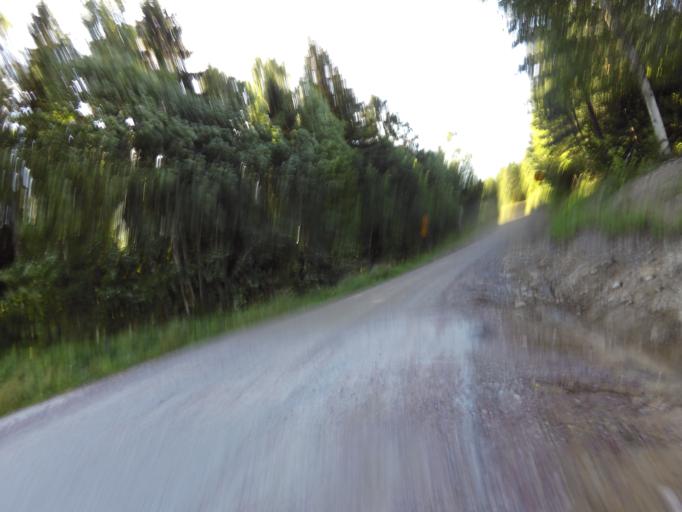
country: SE
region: Gaevleborg
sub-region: Hofors Kommun
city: Hofors
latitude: 60.5675
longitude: 16.2780
